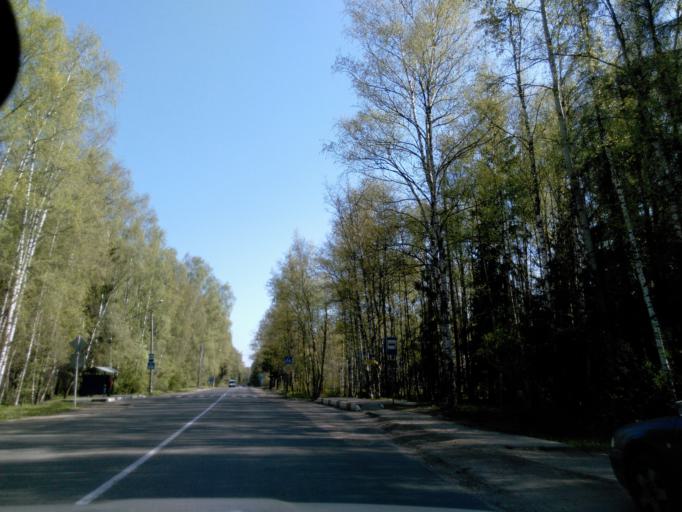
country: RU
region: Moskovskaya
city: Mendeleyevo
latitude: 56.0284
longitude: 37.2184
